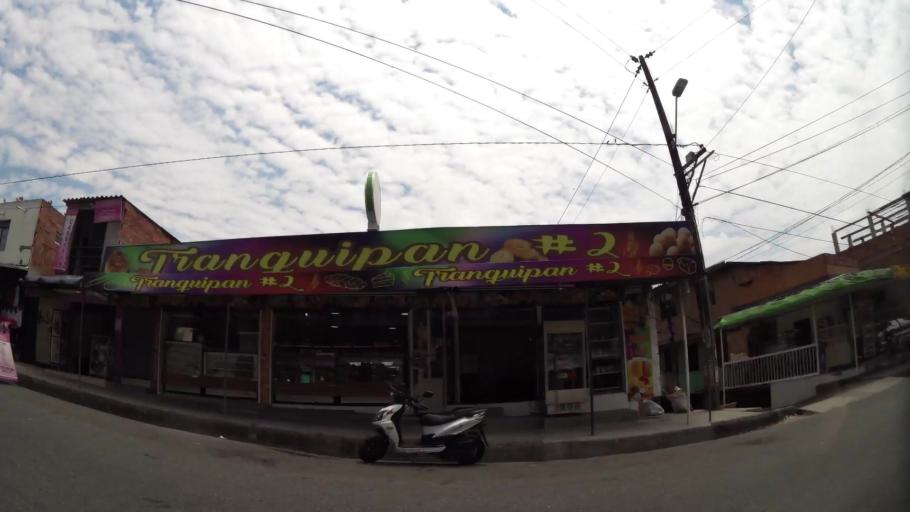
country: CO
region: Antioquia
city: Bello
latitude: 6.3009
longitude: -75.5819
